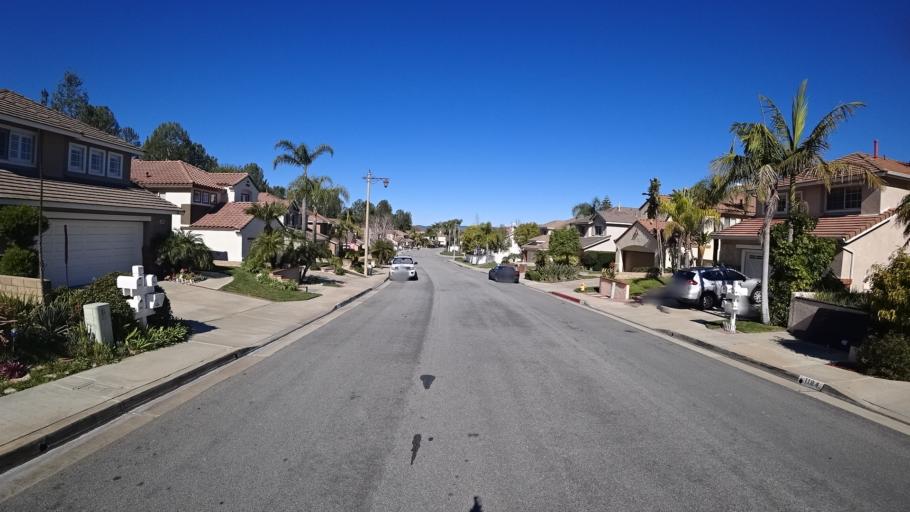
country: US
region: California
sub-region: Orange County
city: Yorba Linda
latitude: 33.8519
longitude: -117.7279
